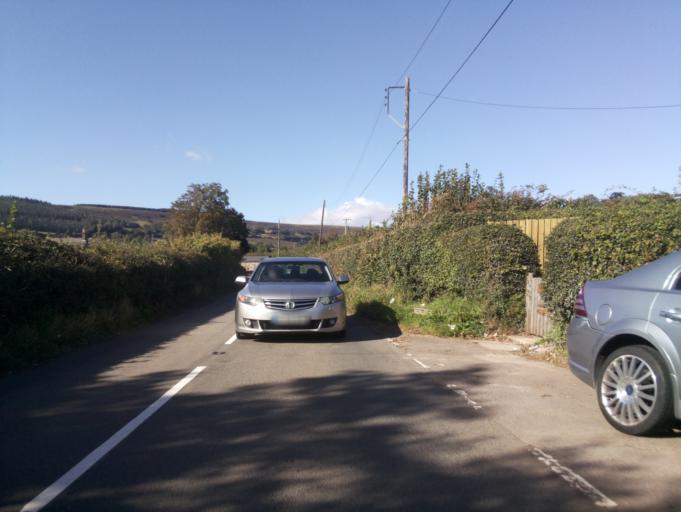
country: GB
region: Wales
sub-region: Torfaen County Borough
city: Cwmbran
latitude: 51.6296
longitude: -3.0507
